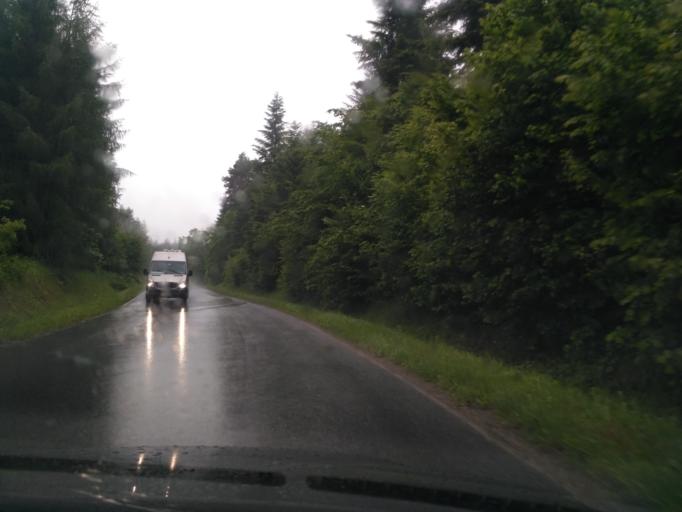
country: PL
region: Subcarpathian Voivodeship
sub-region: Powiat jasielski
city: Debowiec
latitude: 49.6643
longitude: 21.4393
